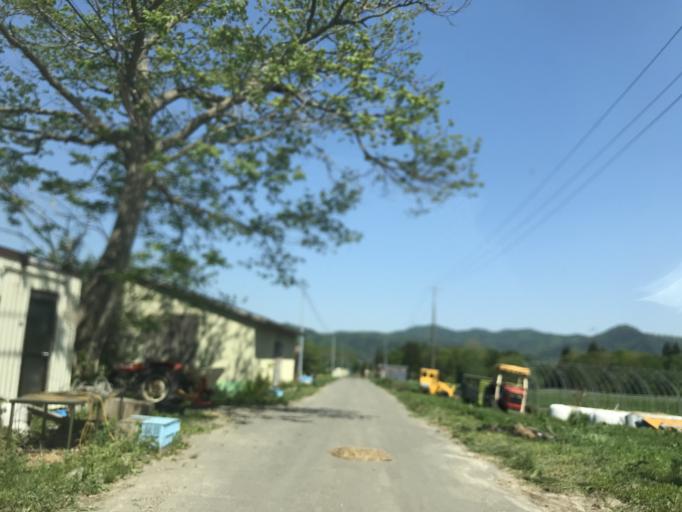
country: JP
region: Iwate
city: Shizukuishi
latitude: 39.5553
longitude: 140.8252
